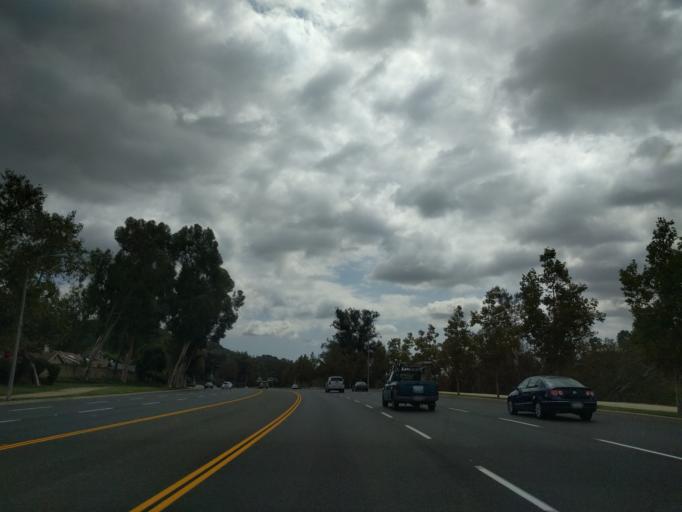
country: US
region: California
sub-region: Orange County
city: Lake Forest
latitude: 33.6525
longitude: -117.6599
